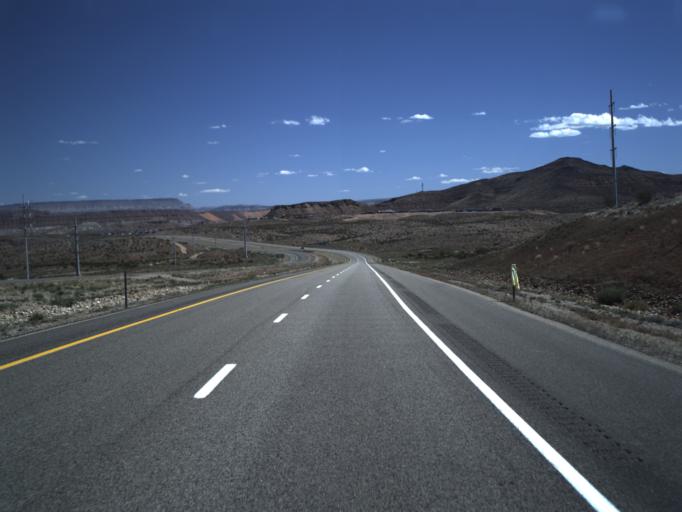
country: US
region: Utah
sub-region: Washington County
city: Saint George
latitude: 37.0051
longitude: -113.5358
